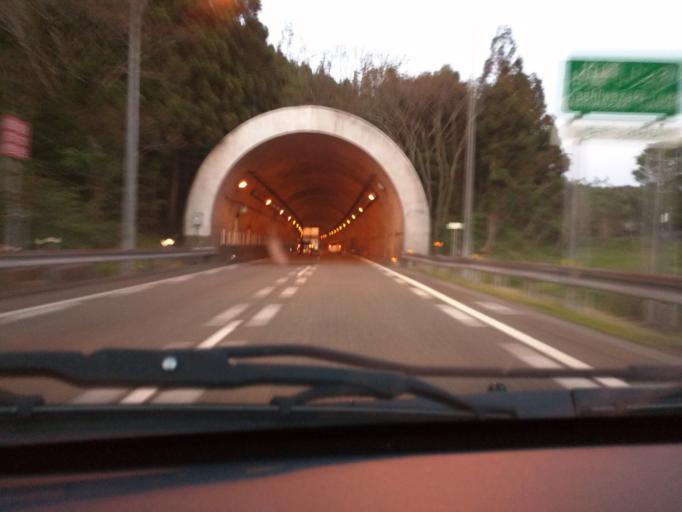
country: JP
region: Niigata
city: Kashiwazaki
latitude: 37.3382
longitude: 138.5360
